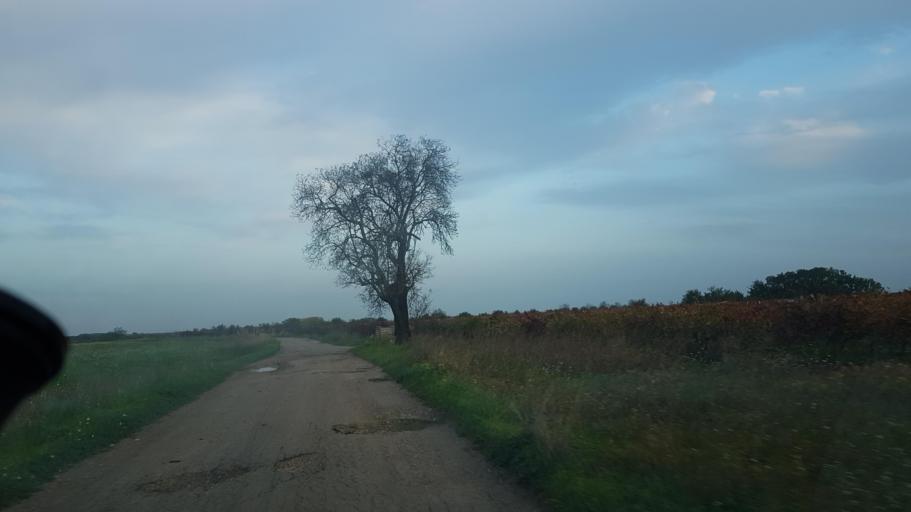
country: IT
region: Apulia
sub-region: Provincia di Brindisi
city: San Donaci
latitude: 40.4261
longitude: 17.9214
